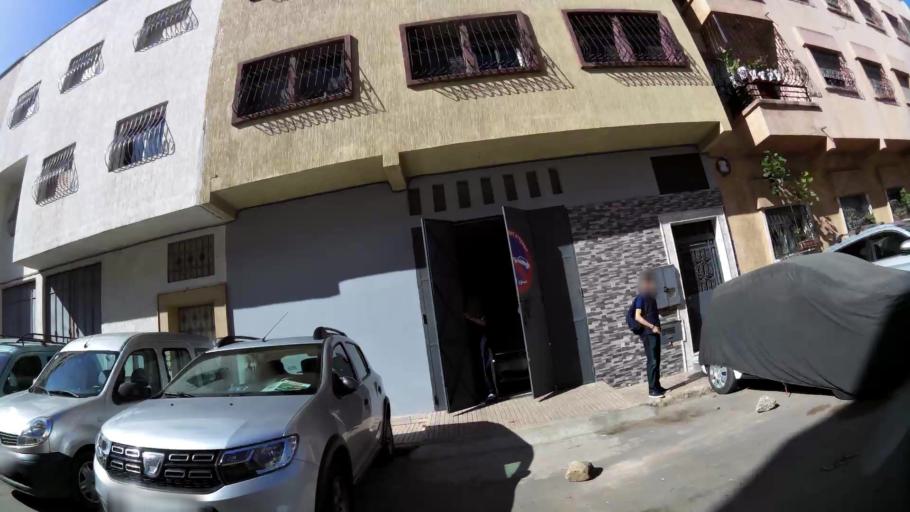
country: MA
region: Rabat-Sale-Zemmour-Zaer
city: Sale
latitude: 34.0554
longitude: -6.8111
